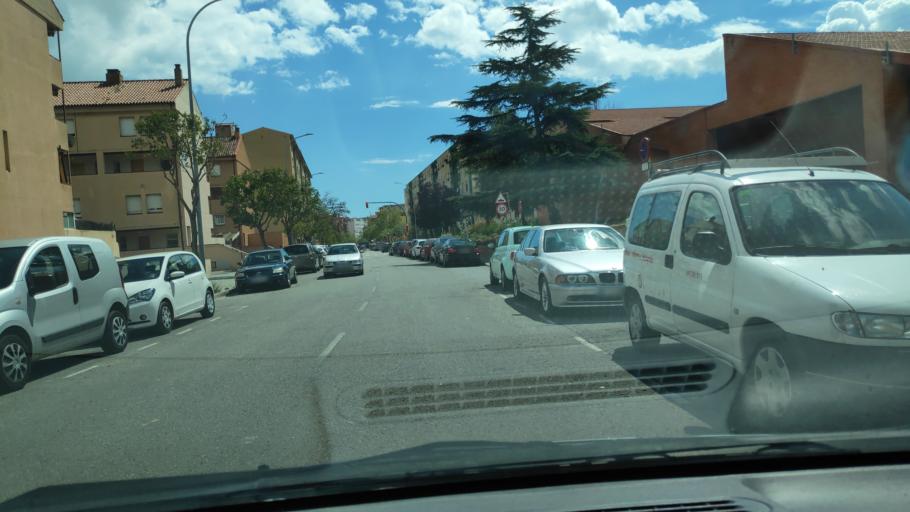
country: ES
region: Catalonia
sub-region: Provincia de Barcelona
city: Sabadell
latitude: 41.5519
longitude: 2.1260
